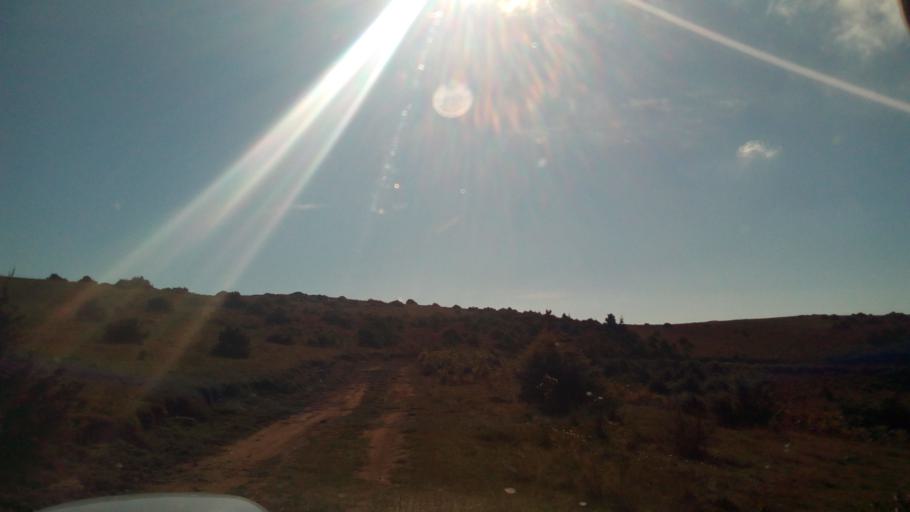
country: GR
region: Central Greece
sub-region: Nomos Fokidos
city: Lidoriki
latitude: 38.6139
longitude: 21.9627
